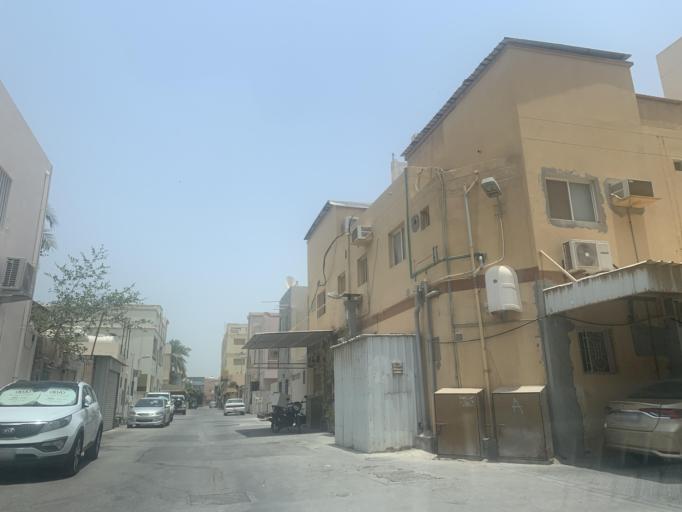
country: BH
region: Manama
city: Jidd Hafs
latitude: 26.2160
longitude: 50.4596
